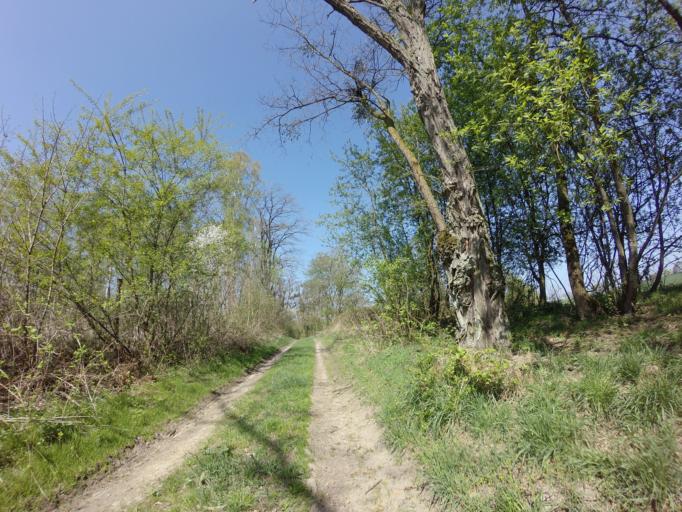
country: PL
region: West Pomeranian Voivodeship
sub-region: Powiat choszczenski
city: Choszczno
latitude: 53.1924
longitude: 15.3701
